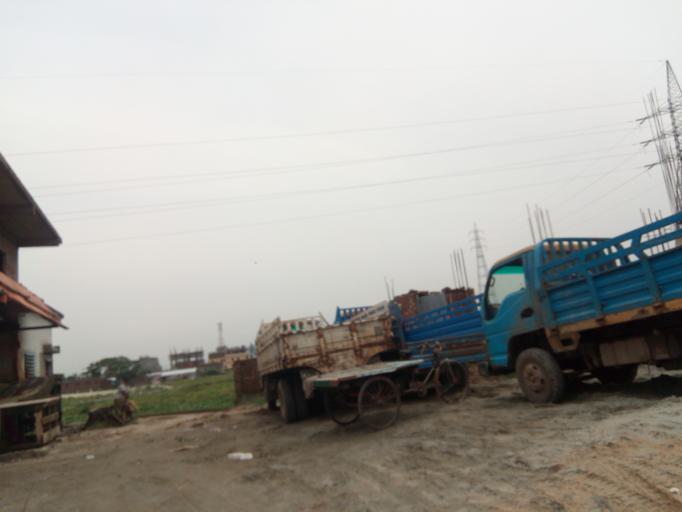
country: BD
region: Dhaka
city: Azimpur
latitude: 23.7438
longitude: 90.3523
